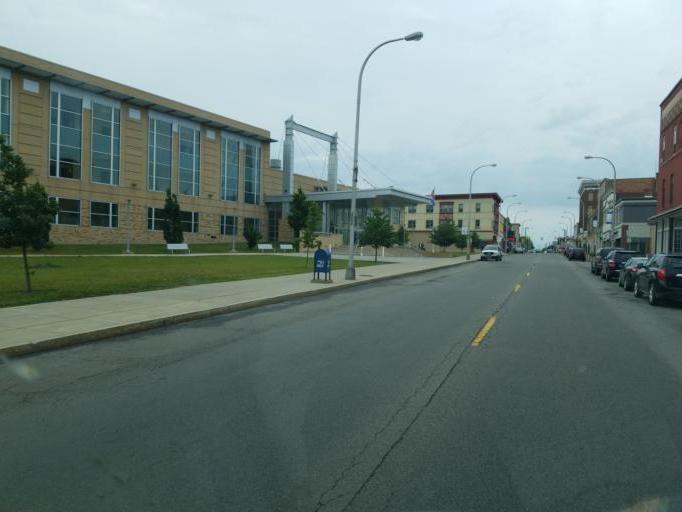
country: US
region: New York
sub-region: Niagara County
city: Niagara Falls
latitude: 43.1066
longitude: -79.0535
